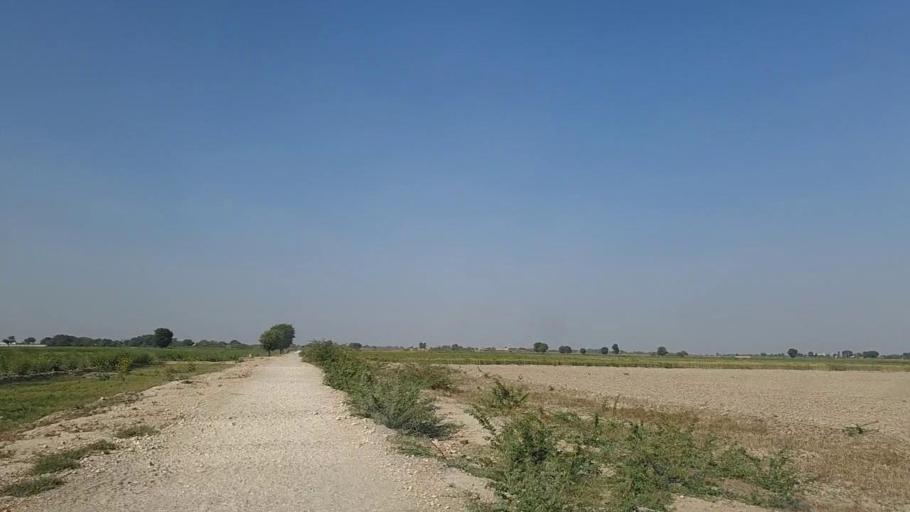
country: PK
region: Sindh
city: Naukot
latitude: 24.9402
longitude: 69.4839
